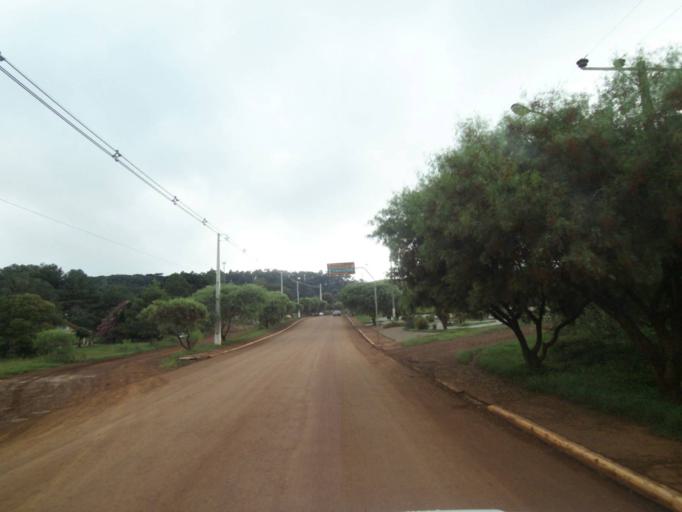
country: BR
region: Parana
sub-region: Pitanga
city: Pitanga
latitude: -24.9402
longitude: -51.8674
